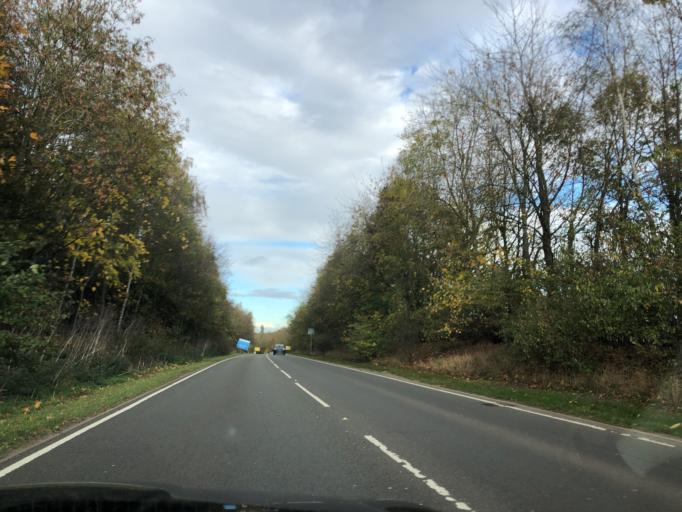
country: GB
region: England
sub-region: Warwickshire
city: Warwick
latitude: 52.2584
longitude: -1.5629
